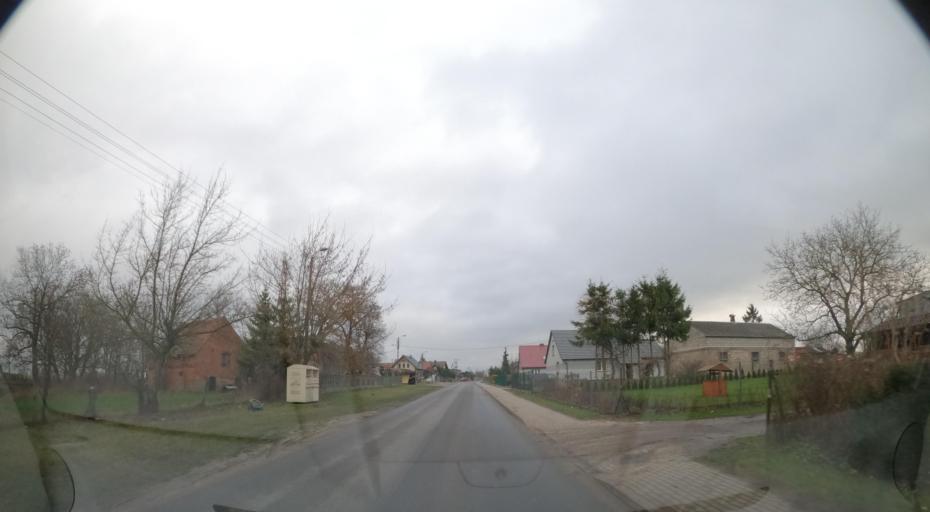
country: PL
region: Greater Poland Voivodeship
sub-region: Powiat pilski
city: Lobzenica
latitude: 53.2300
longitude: 17.3164
